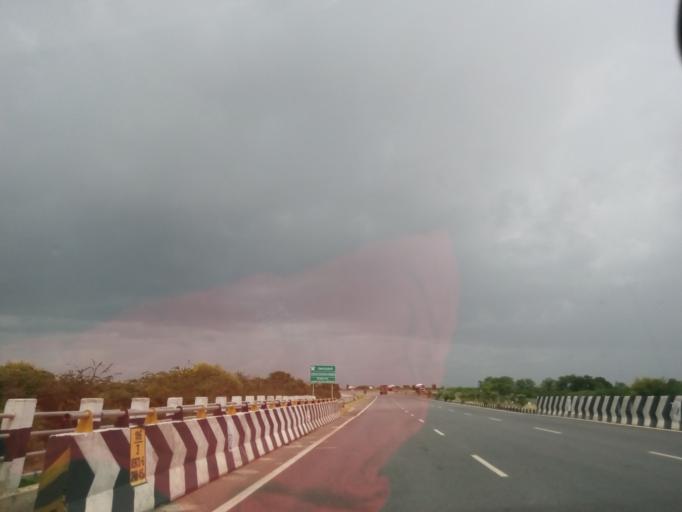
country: IN
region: Karnataka
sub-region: Chitradurga
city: Chitradurga
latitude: 14.1427
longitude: 76.4908
